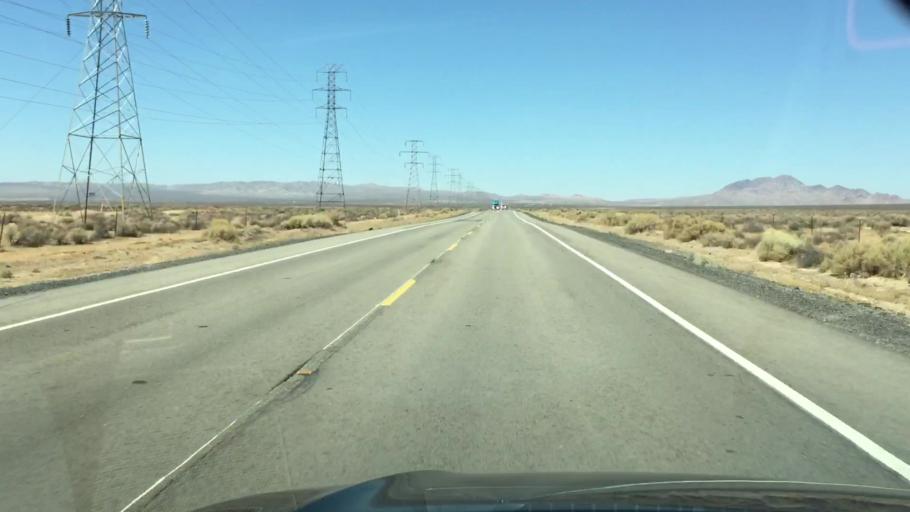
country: US
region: California
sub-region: Kern County
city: Boron
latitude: 35.1849
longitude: -117.5953
